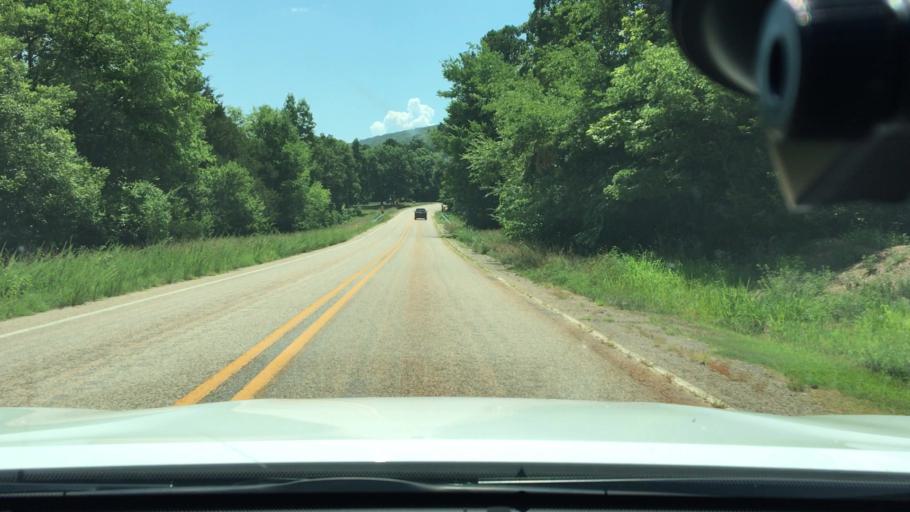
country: US
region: Arkansas
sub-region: Logan County
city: Paris
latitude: 35.1912
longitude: -93.6248
